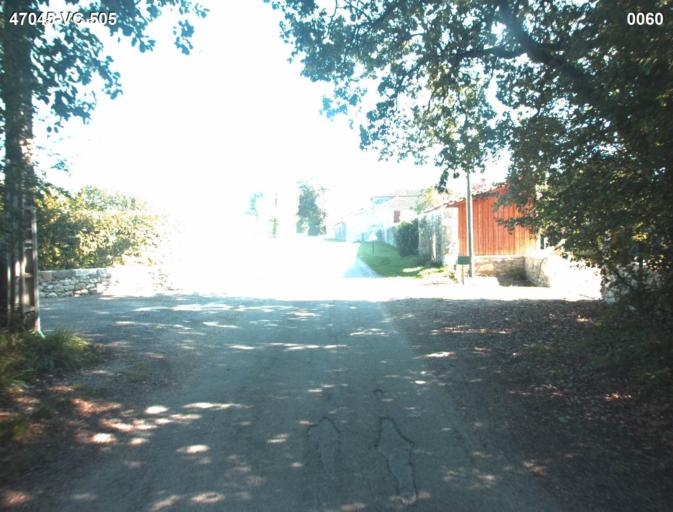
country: FR
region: Aquitaine
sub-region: Departement du Lot-et-Garonne
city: Nerac
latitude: 44.1501
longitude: 0.3986
